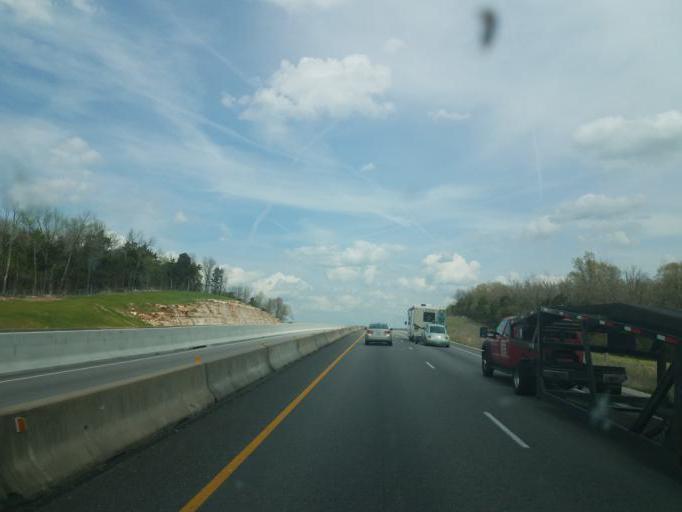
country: US
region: Kentucky
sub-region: Hart County
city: Munfordville
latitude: 37.4456
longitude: -85.8836
